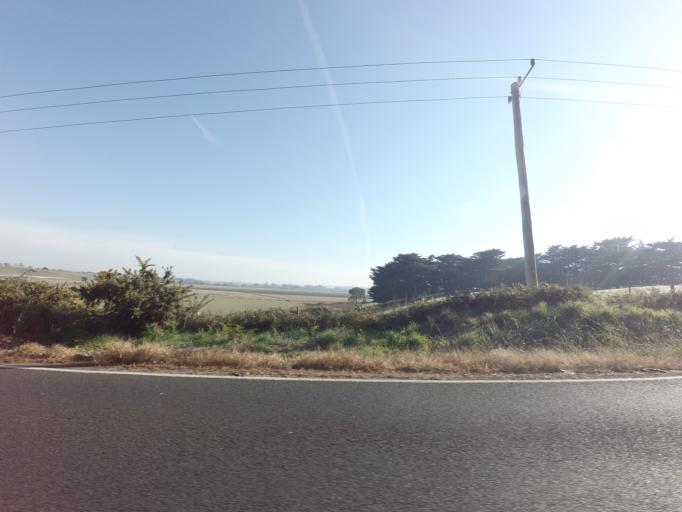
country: AU
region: Tasmania
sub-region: Launceston
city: Summerhill
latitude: -41.5273
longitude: 147.0222
